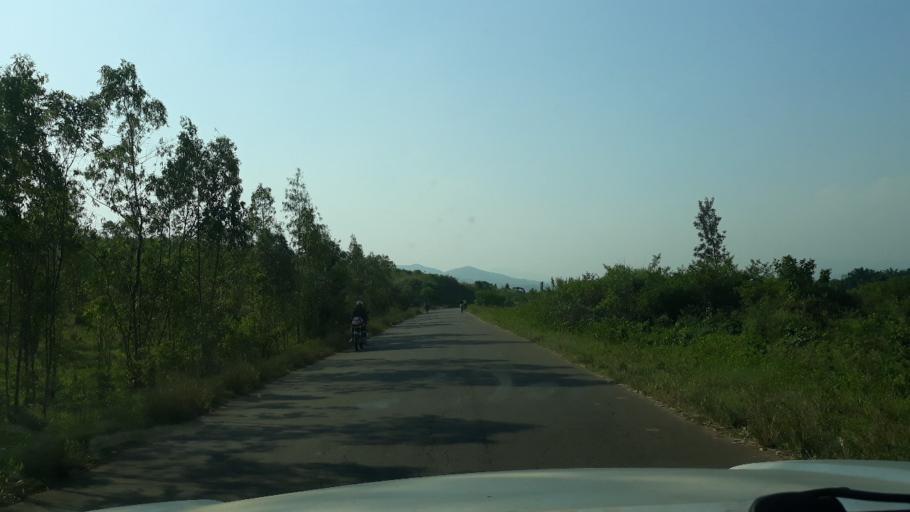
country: BI
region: Cibitoke
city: Cibitoke
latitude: -2.7755
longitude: 28.9990
